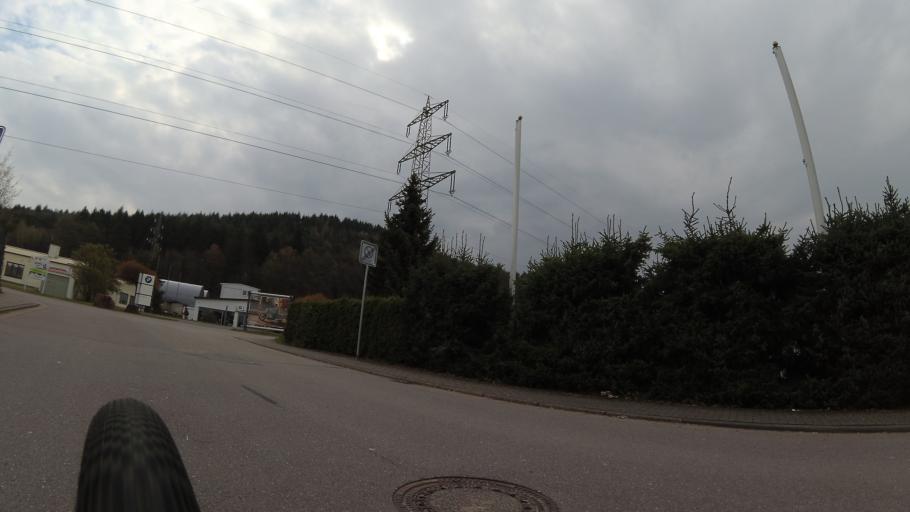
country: DE
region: Saarland
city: Merzig
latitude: 49.4656
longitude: 6.6258
